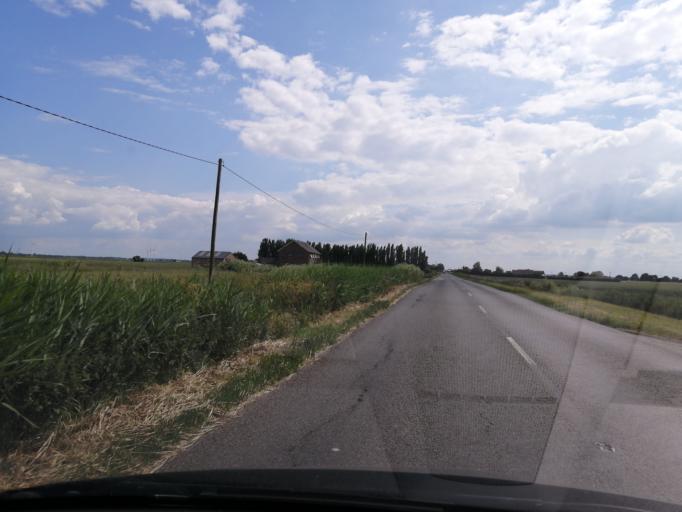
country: GB
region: England
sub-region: Cambridgeshire
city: Whittlesey
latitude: 52.5054
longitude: -0.1448
